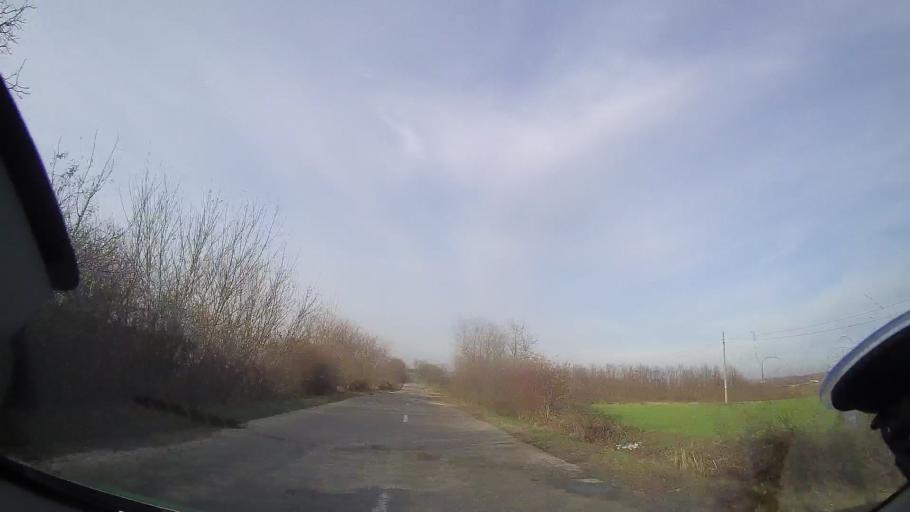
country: RO
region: Bihor
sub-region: Comuna Spinus
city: Spinus
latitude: 47.2107
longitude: 22.1790
